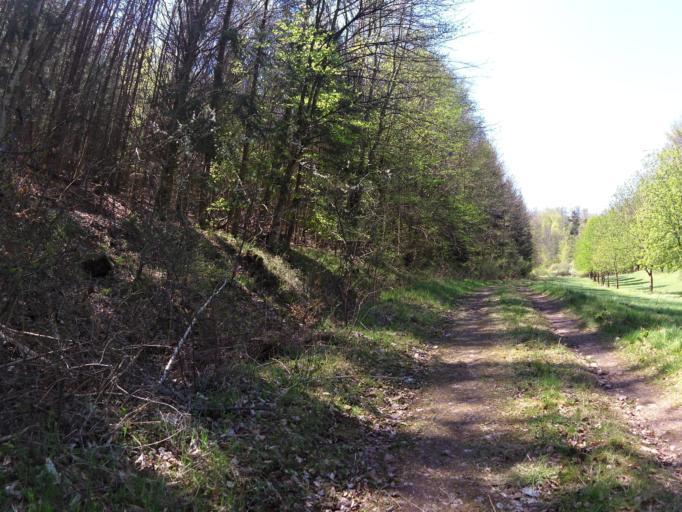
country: DE
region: Thuringia
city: Krauthausen
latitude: 50.9837
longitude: 10.2398
